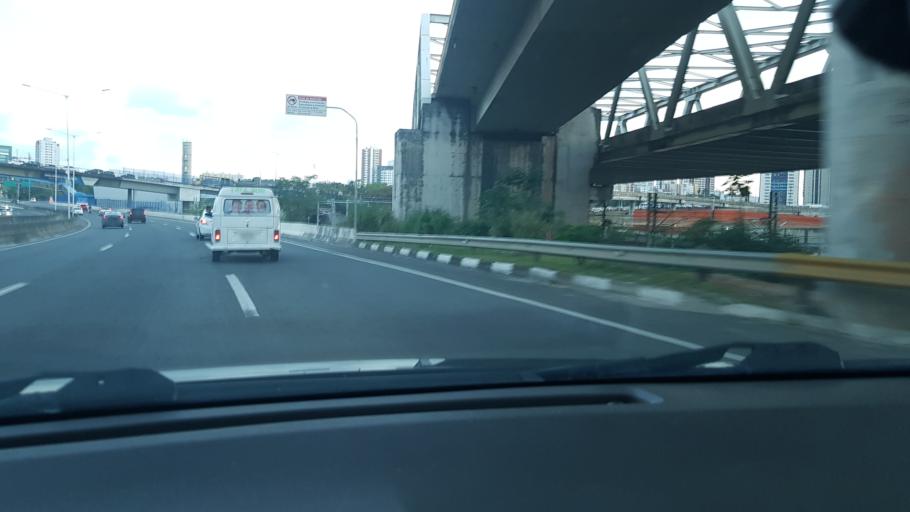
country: BR
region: Bahia
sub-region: Salvador
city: Salvador
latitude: -12.9661
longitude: -38.4772
